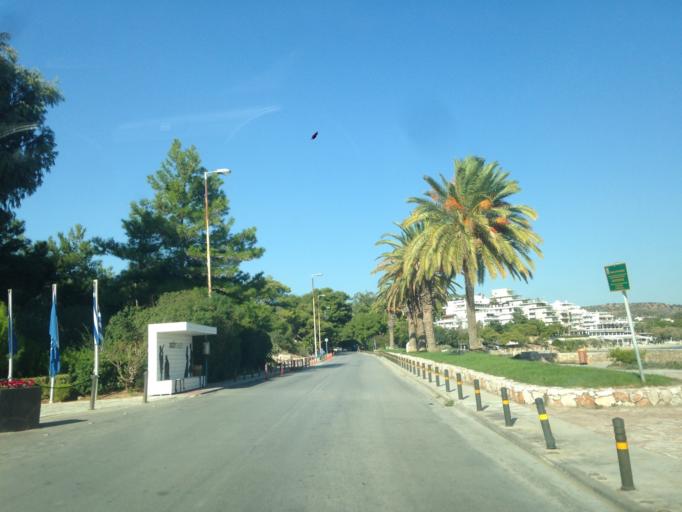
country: GR
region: Attica
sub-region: Nomarchia Anatolikis Attikis
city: Vouliagmeni
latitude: 37.8102
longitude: 23.7741
